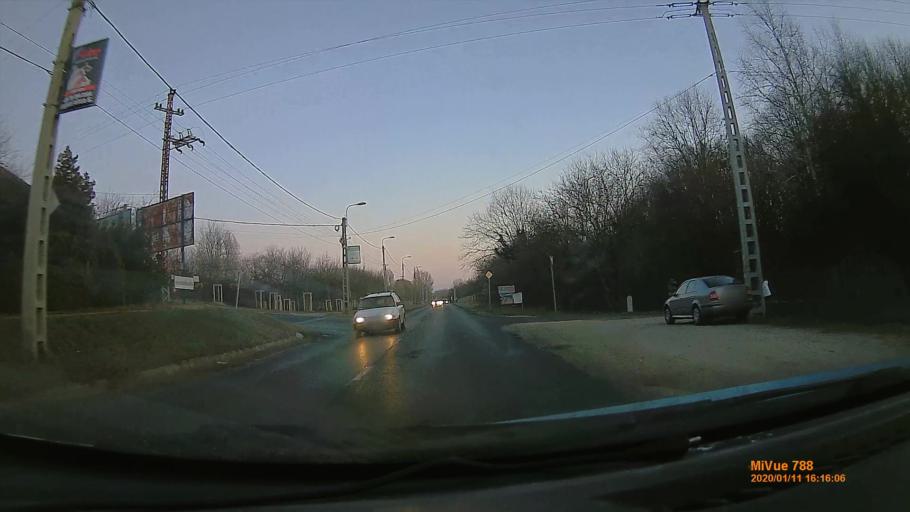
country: HU
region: Budapest
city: Budapest XVI. keruelet
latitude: 47.5280
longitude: 19.1974
